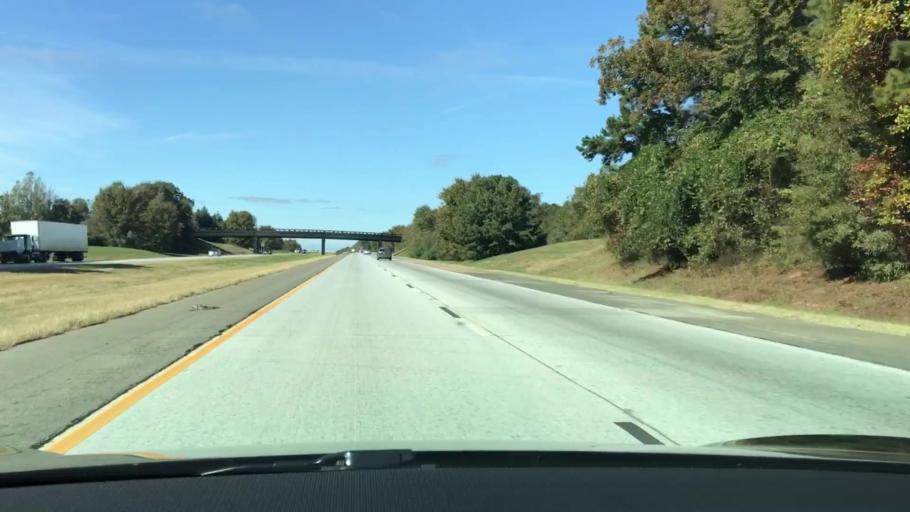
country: US
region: Georgia
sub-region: Putnam County
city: Jefferson
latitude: 33.5391
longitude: -83.3119
